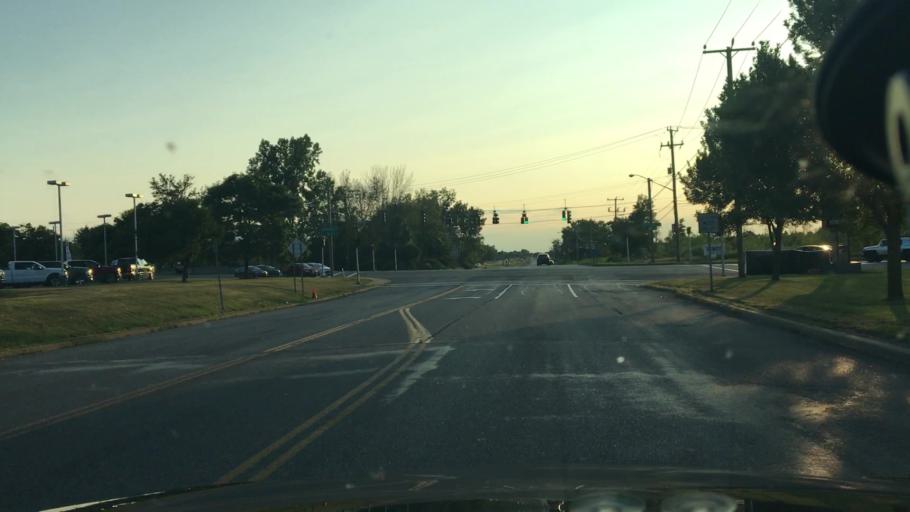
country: US
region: New York
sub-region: Erie County
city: Orchard Park
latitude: 42.7891
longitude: -78.7592
